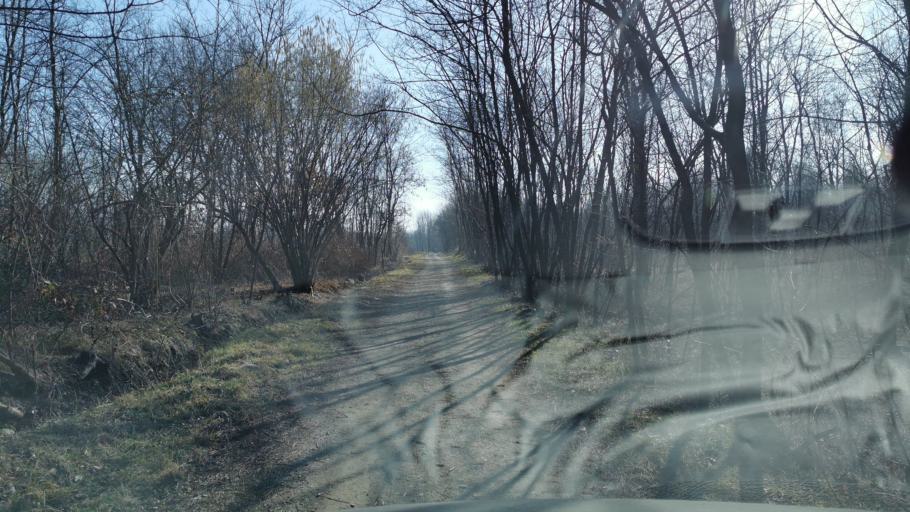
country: IT
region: Piedmont
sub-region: Provincia di Torino
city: Robassomero
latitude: 45.2169
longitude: 7.5678
